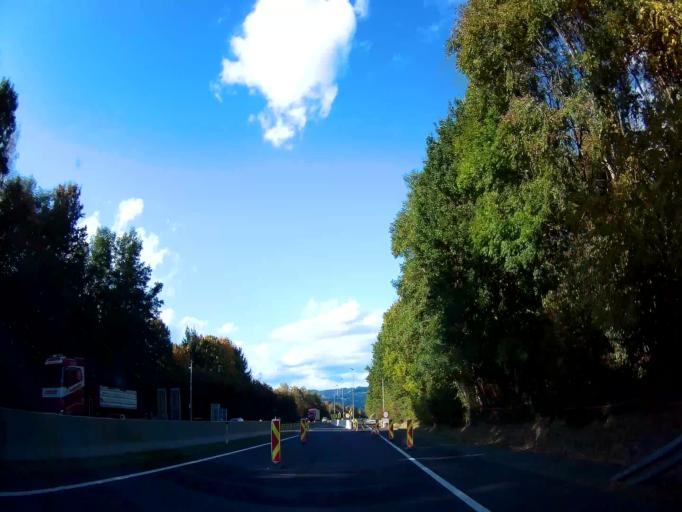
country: AT
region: Carinthia
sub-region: Politischer Bezirk Wolfsberg
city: Wolfsberg
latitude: 46.8223
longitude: 14.8205
